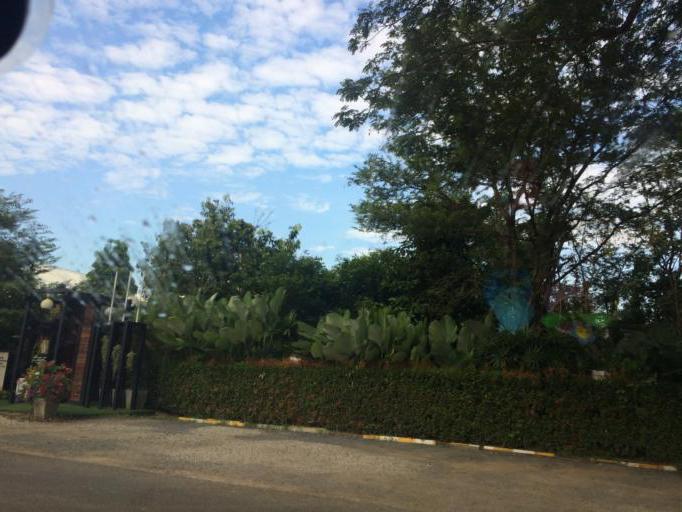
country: TH
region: Chiang Mai
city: San Sai
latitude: 18.8292
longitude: 99.0201
